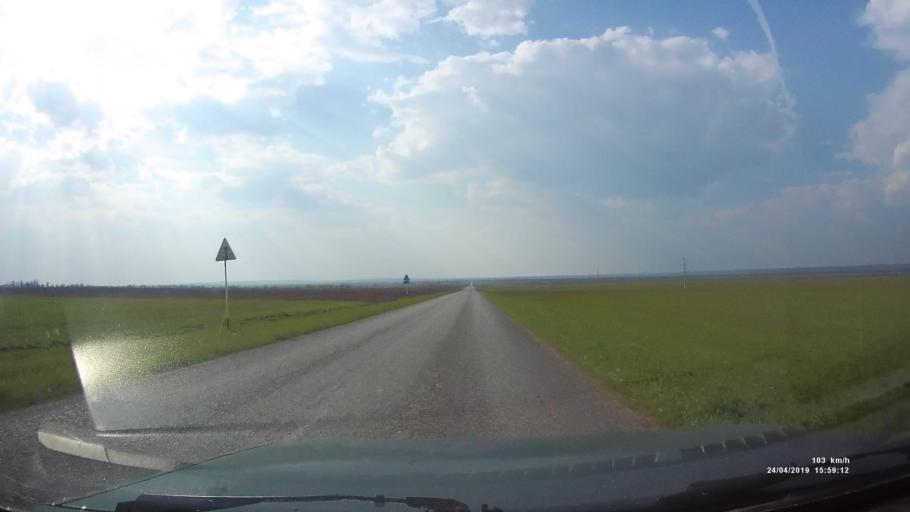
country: RU
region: Rostov
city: Sovetskoye
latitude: 46.6211
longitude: 42.4765
